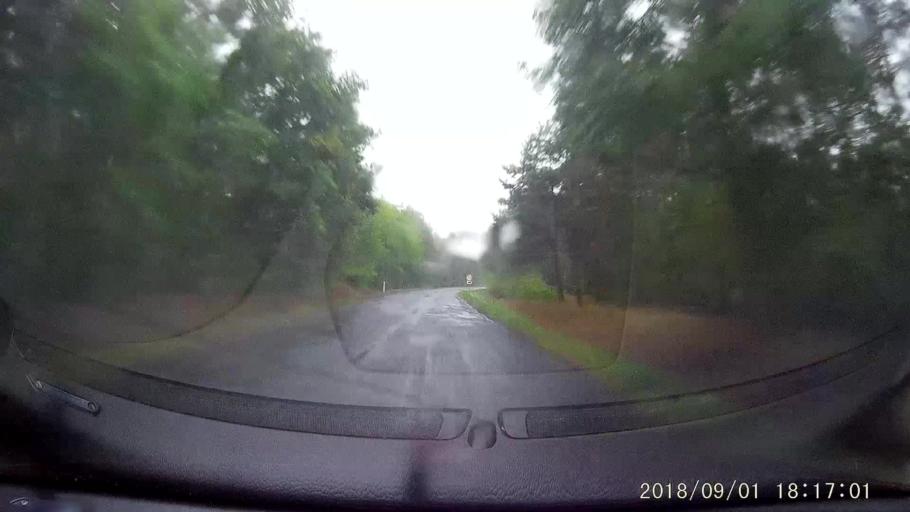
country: PL
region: Lower Silesian Voivodeship
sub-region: Powiat zgorzelecki
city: Piensk
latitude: 51.2662
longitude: 15.0513
